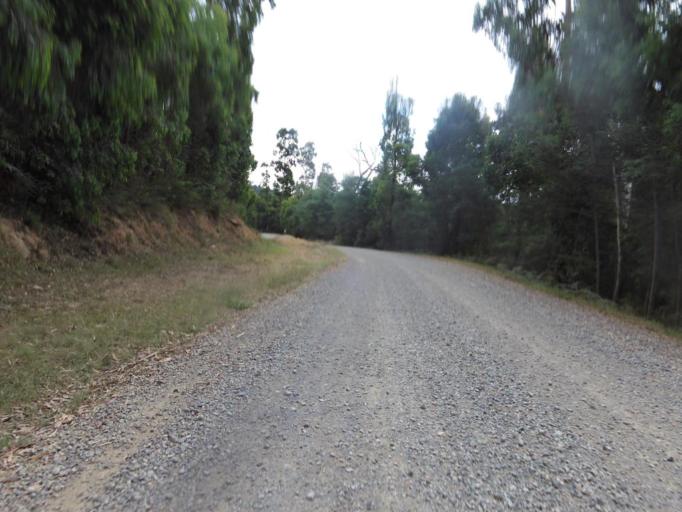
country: AU
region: Victoria
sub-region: Yarra Ranges
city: Healesville
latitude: -37.4146
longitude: 145.5640
